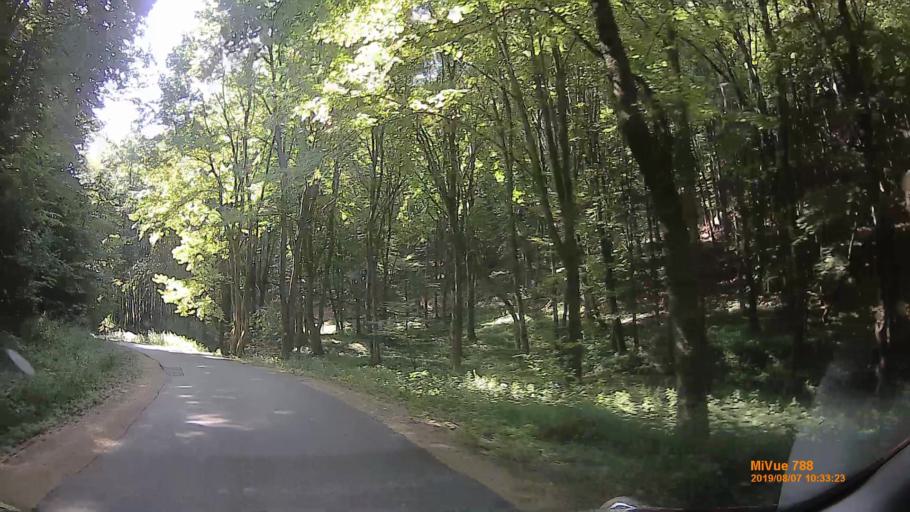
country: HU
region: Veszprem
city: Ajka
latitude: 47.0643
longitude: 17.5922
